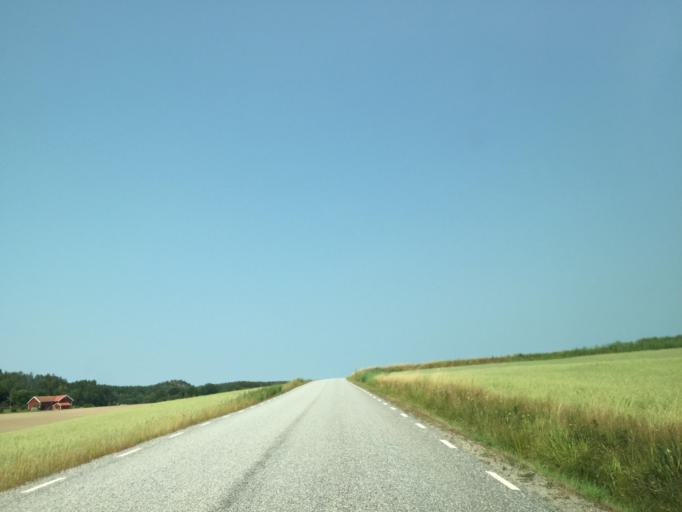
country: SE
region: Vaestra Goetaland
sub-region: Lilla Edets Kommun
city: Lilla Edet
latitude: 58.2011
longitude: 12.1228
